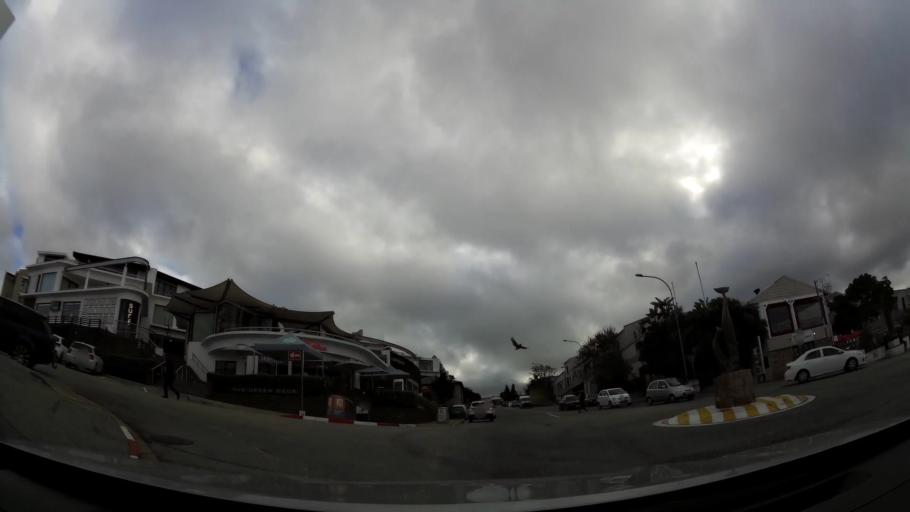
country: ZA
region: Western Cape
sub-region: Eden District Municipality
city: Plettenberg Bay
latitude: -34.0565
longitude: 23.3722
